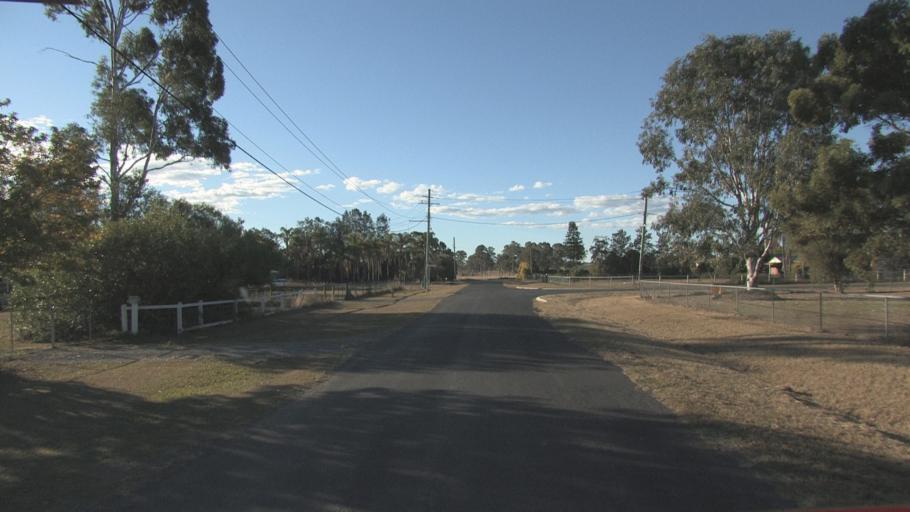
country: AU
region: Queensland
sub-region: Logan
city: Cedar Vale
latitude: -27.8623
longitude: 152.9661
